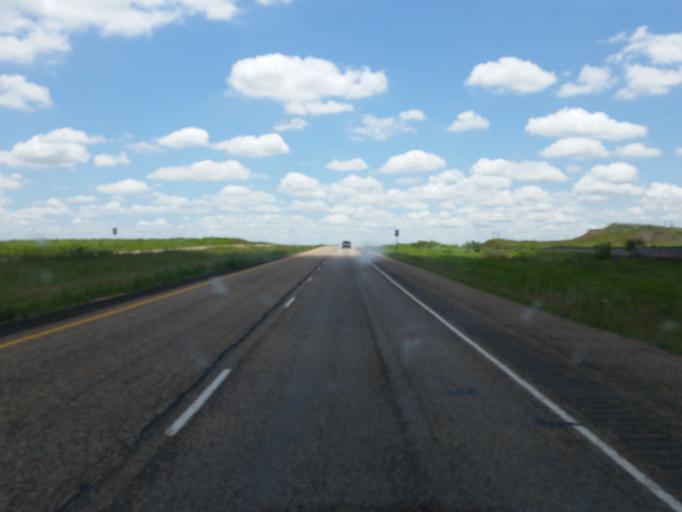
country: US
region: Texas
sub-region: Garza County
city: Post
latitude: 33.1207
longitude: -101.2828
